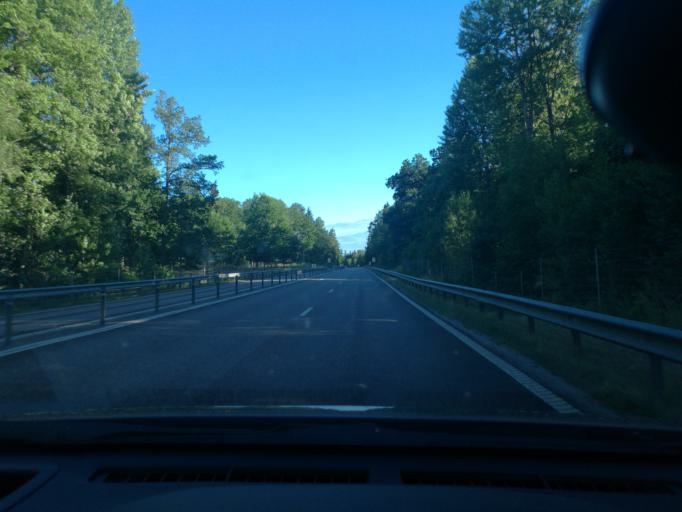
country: SE
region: Kalmar
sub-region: Monsteras Kommun
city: Timmernabben
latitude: 56.9088
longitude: 16.3813
